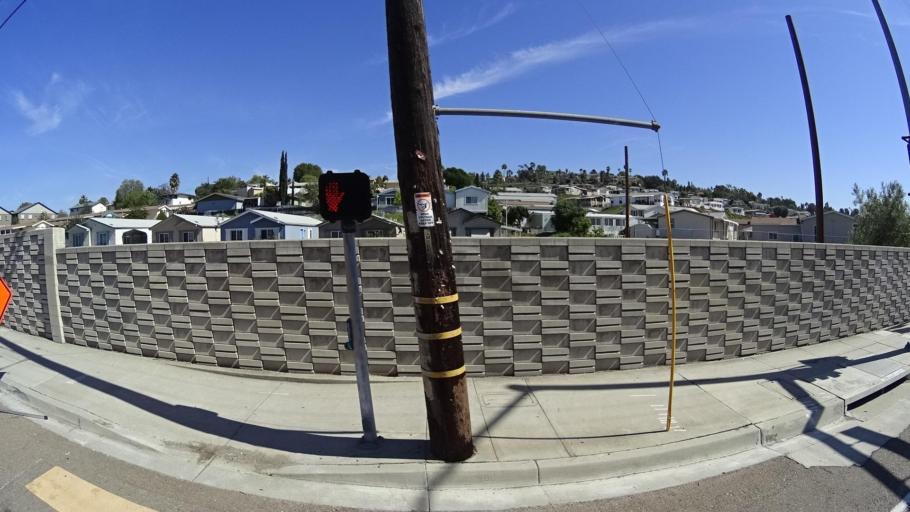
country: US
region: California
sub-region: San Diego County
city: La Presa
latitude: 32.7250
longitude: -117.0141
